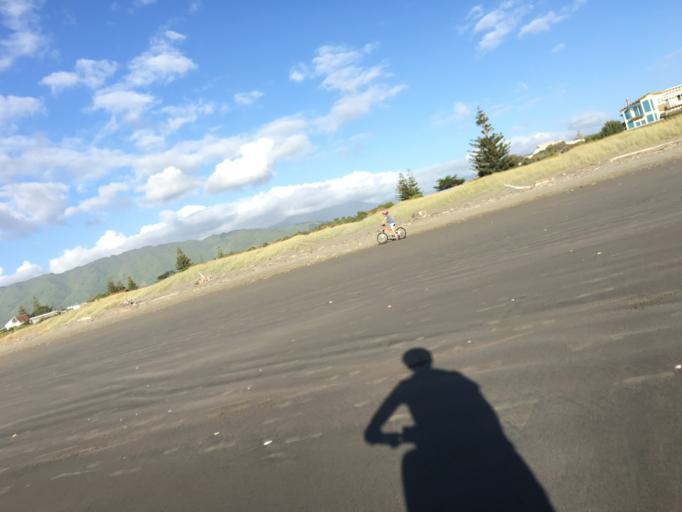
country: NZ
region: Wellington
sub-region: Kapiti Coast District
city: Paraparaumu
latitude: -40.8581
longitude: 175.0264
